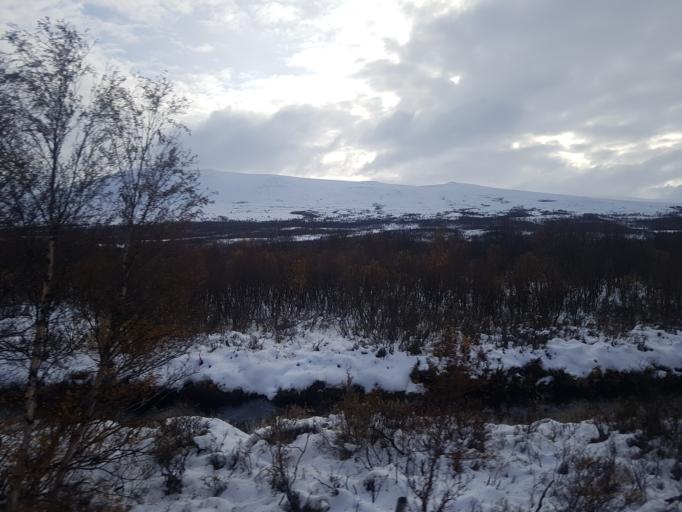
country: NO
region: Oppland
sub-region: Dovre
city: Dovre
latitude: 62.1246
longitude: 9.3023
